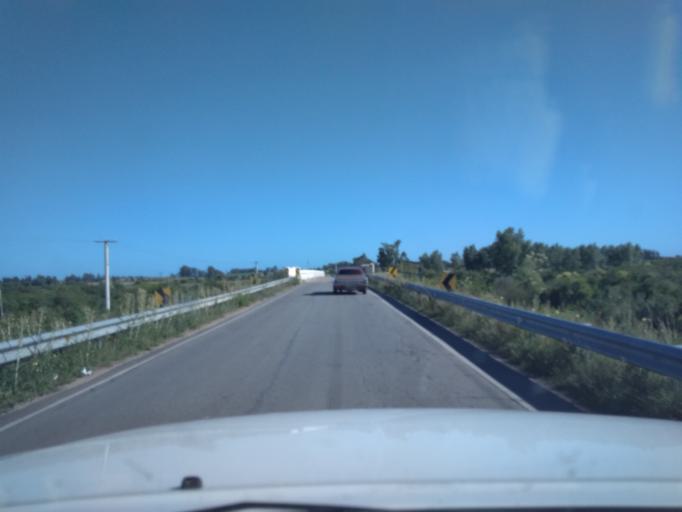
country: UY
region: Canelones
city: San Ramon
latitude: -34.3242
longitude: -55.9614
